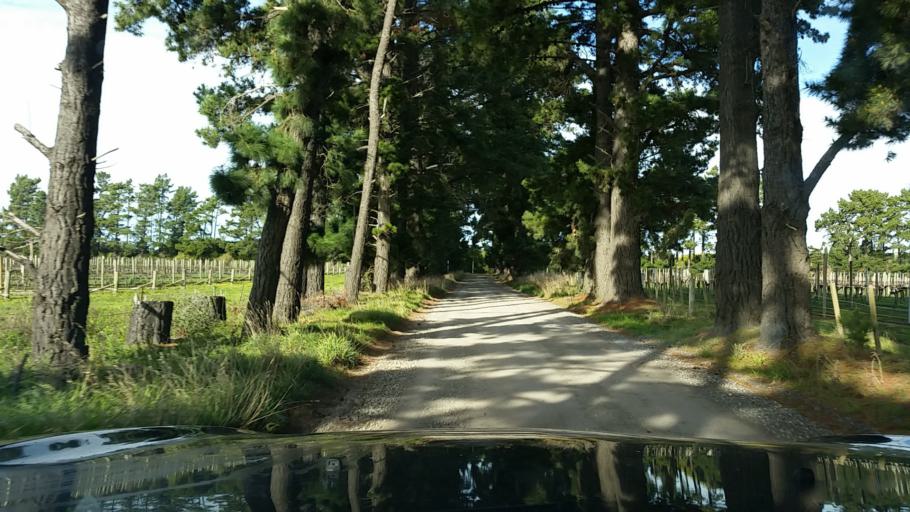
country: NZ
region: Marlborough
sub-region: Marlborough District
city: Blenheim
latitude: -41.6288
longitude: 174.1022
